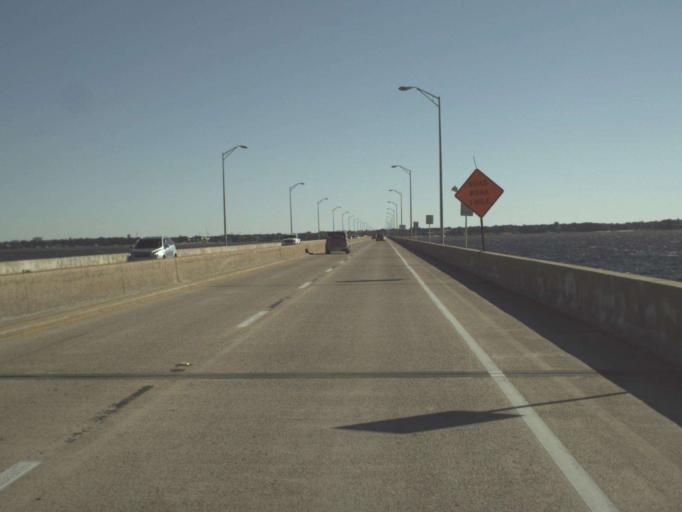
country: US
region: Florida
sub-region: Santa Rosa County
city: Gulf Breeze
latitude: 30.3879
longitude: -87.1826
